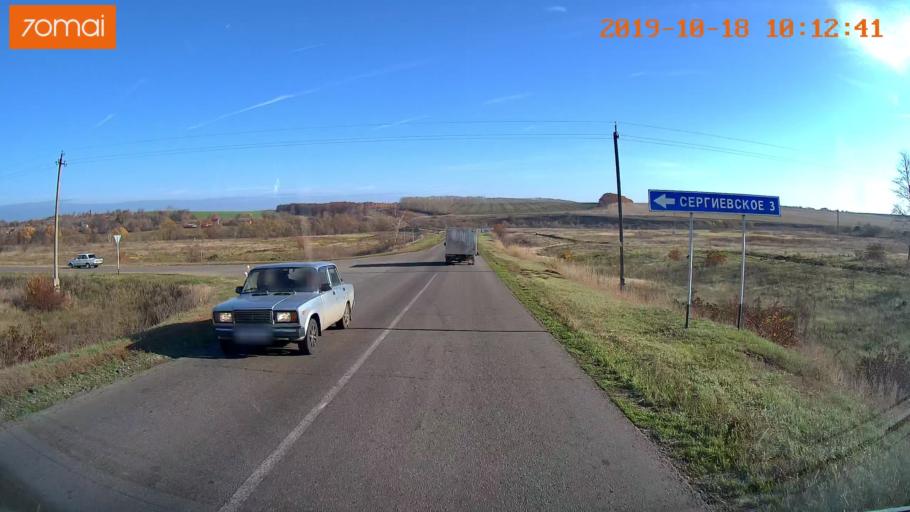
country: RU
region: Tula
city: Kurkino
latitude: 53.3960
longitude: 38.5107
